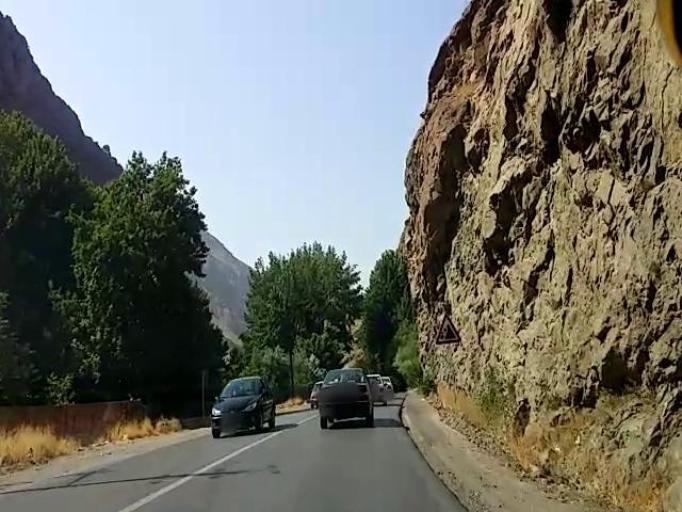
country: IR
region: Alborz
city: Karaj
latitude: 35.8947
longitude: 51.0456
